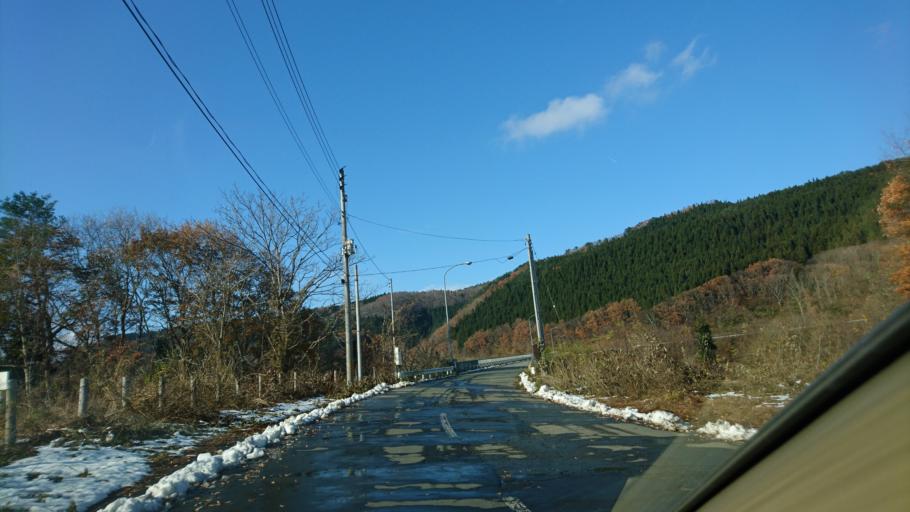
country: JP
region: Akita
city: Yokotemachi
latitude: 39.2997
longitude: 140.8289
